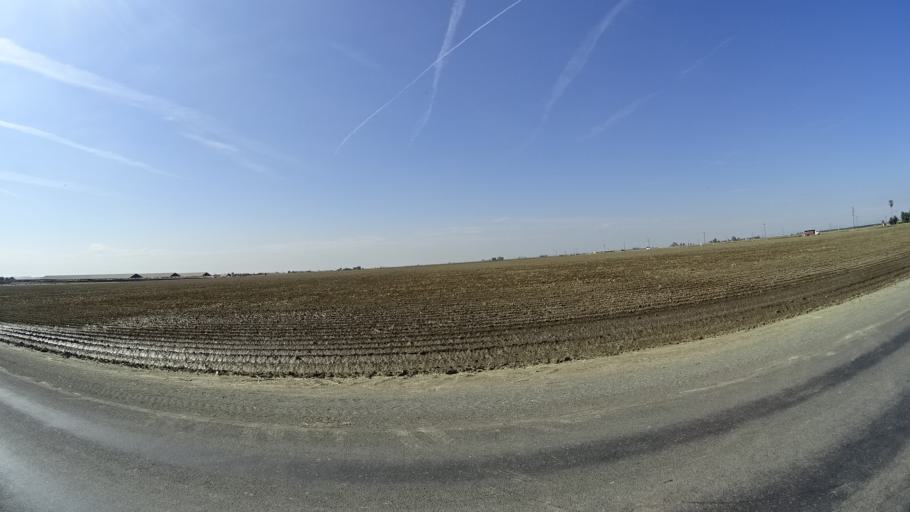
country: US
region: California
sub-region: Kings County
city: Home Garden
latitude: 36.2549
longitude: -119.5800
